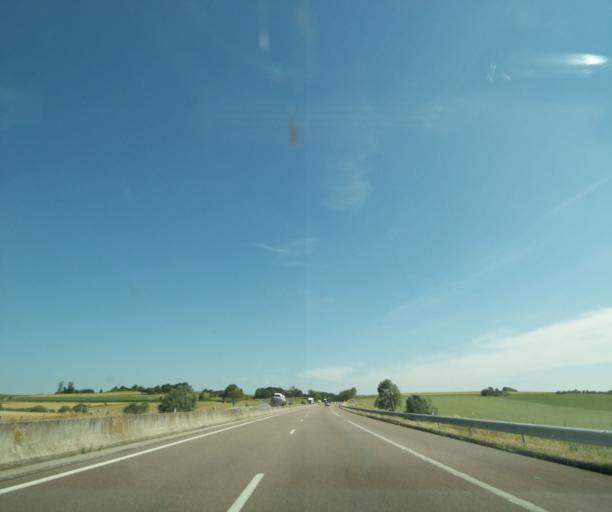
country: FR
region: Lorraine
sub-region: Departement des Vosges
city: Chatenois
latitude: 48.3931
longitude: 5.8799
